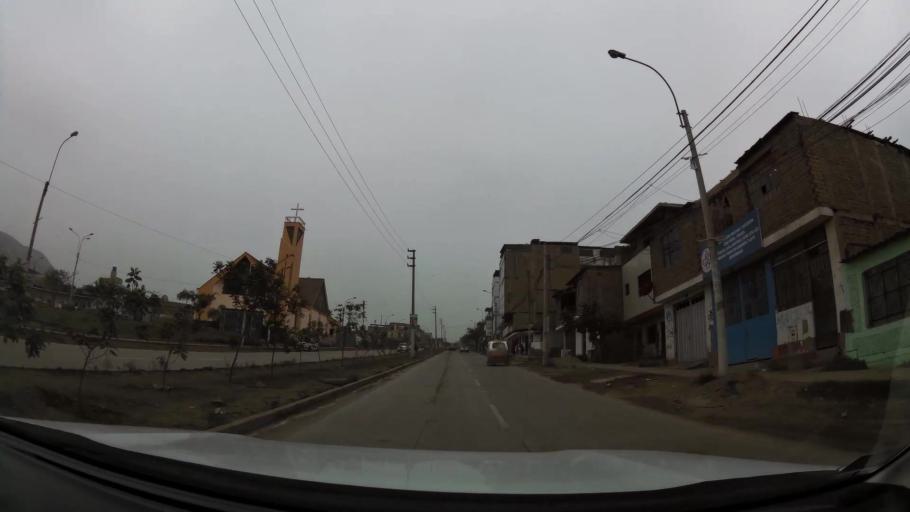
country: PE
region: Lima
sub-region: Lima
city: Surco
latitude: -12.1916
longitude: -76.9331
